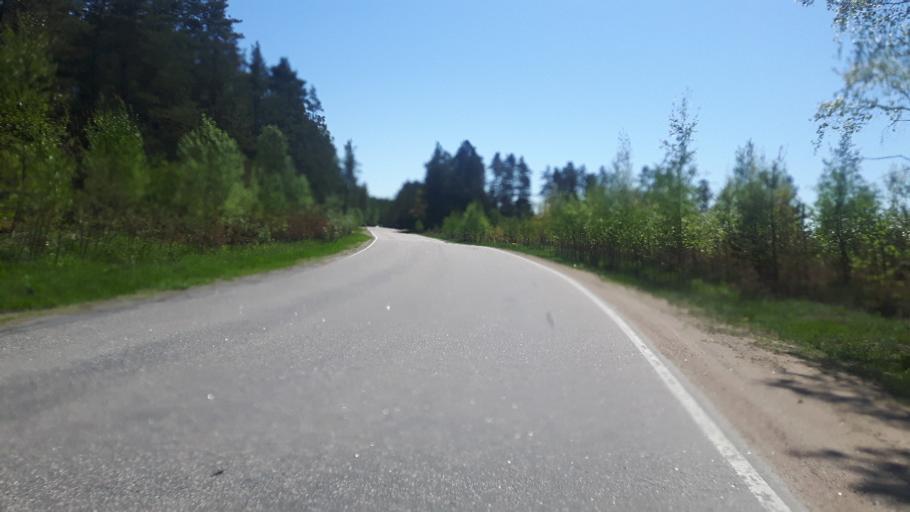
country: RU
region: Leningrad
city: Glebychevo
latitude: 60.3337
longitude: 28.8204
